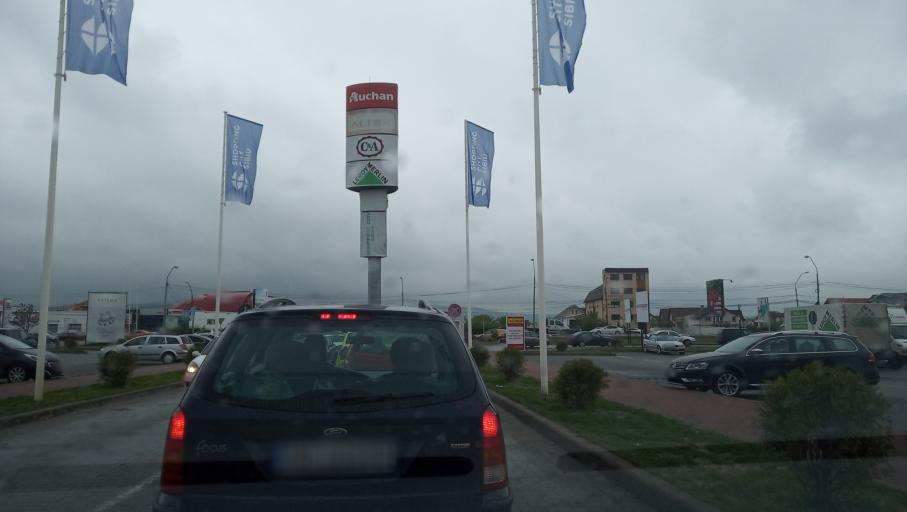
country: RO
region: Sibiu
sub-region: Comuna Selimbar
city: Selimbar
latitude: 45.7766
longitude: 24.1710
